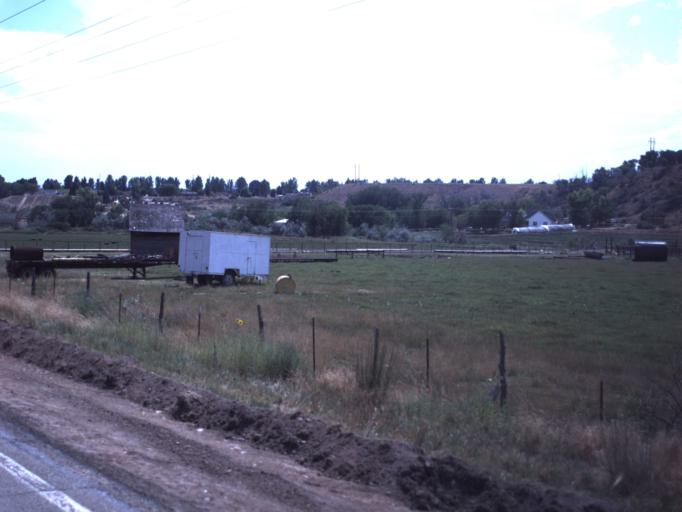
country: US
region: Utah
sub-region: Duchesne County
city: Roosevelt
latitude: 40.3192
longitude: -110.0147
